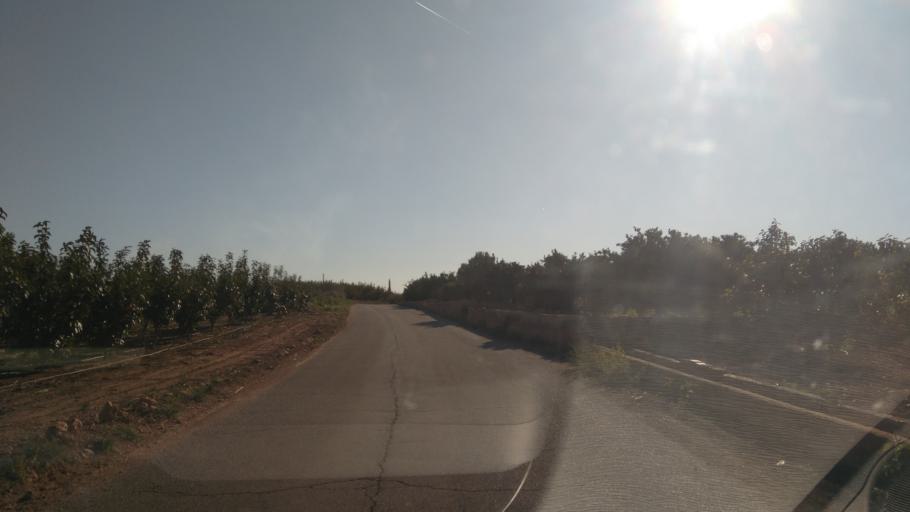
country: ES
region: Valencia
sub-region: Provincia de Valencia
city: Benimodo
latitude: 39.1815
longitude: -0.5306
